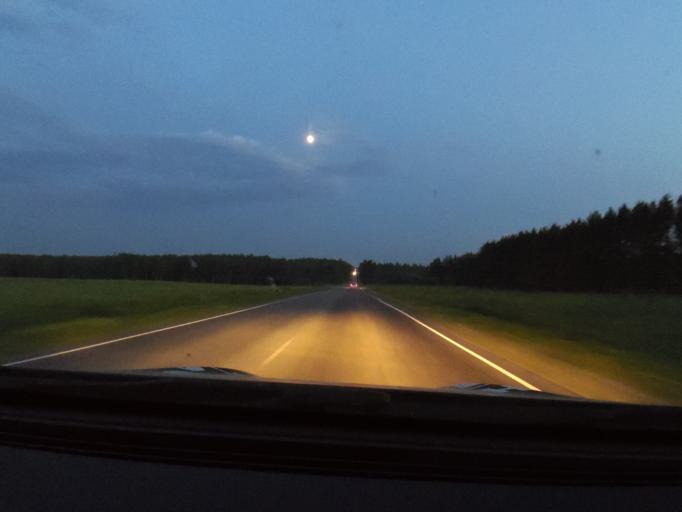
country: RU
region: Bashkortostan
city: Duvan
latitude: 56.0153
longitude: 58.2130
